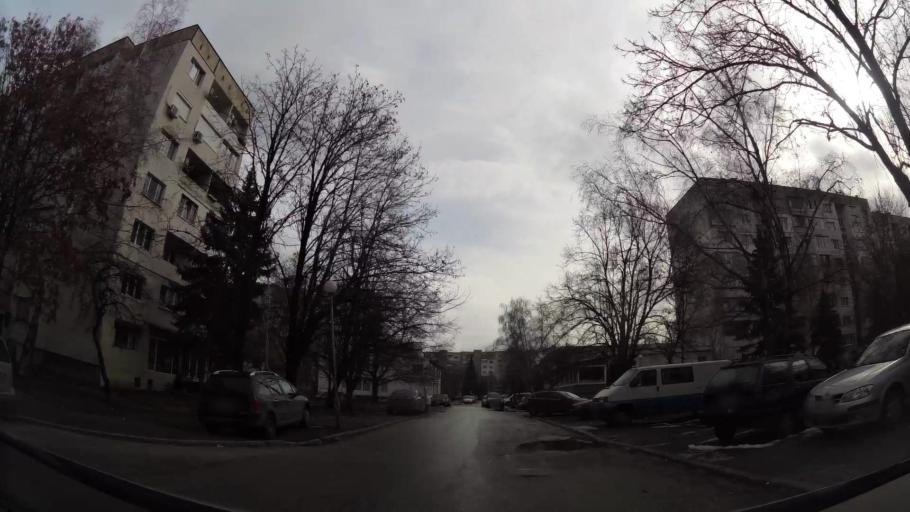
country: BG
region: Sofiya
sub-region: Obshtina Bozhurishte
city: Bozhurishte
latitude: 42.7155
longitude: 23.2482
